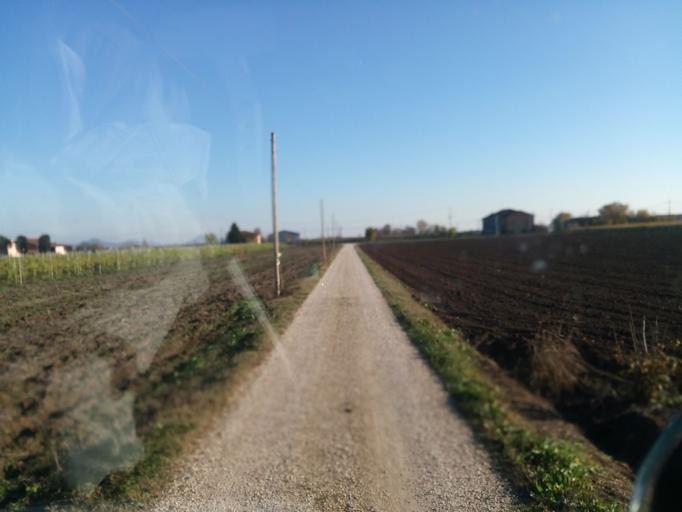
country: IT
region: Veneto
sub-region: Provincia di Vicenza
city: Asigliano Veneto
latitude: 45.3293
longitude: 11.4244
